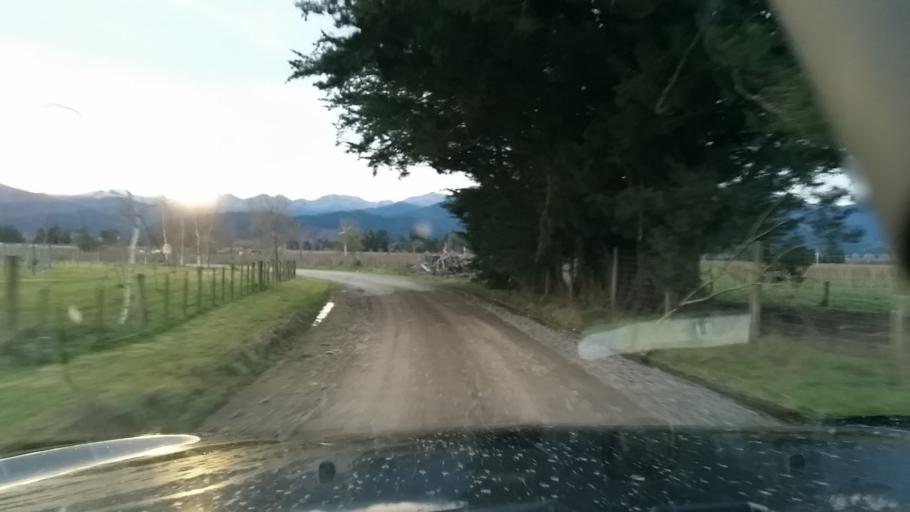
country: NZ
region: Nelson
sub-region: Nelson City
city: Nelson
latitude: -41.5822
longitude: 173.5091
